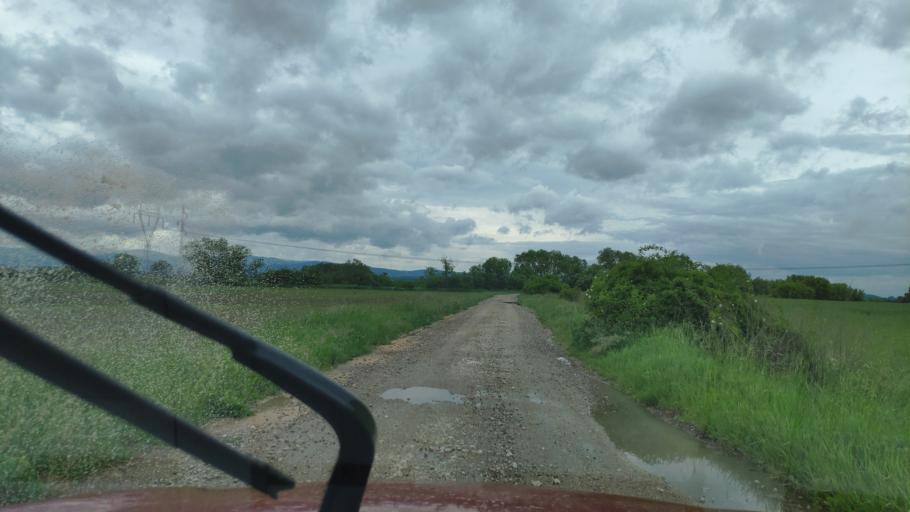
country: SK
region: Kosicky
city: Moldava nad Bodvou
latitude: 48.5600
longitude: 21.1162
